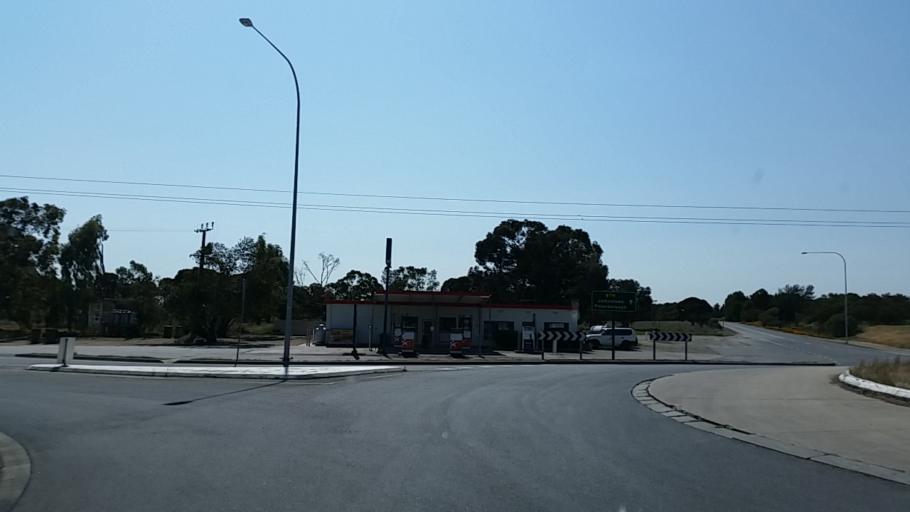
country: AU
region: South Australia
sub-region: Port Pirie City and Dists
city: Crystal Brook
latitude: -33.2648
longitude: 138.3455
